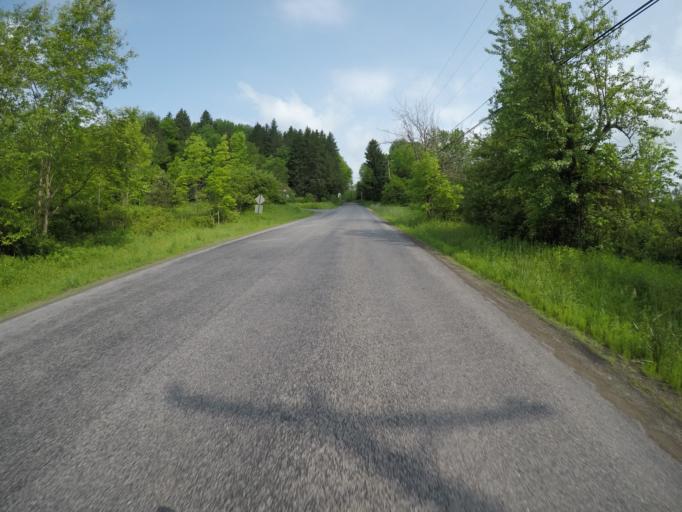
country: US
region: New York
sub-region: Delaware County
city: Stamford
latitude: 42.1562
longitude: -74.6549
